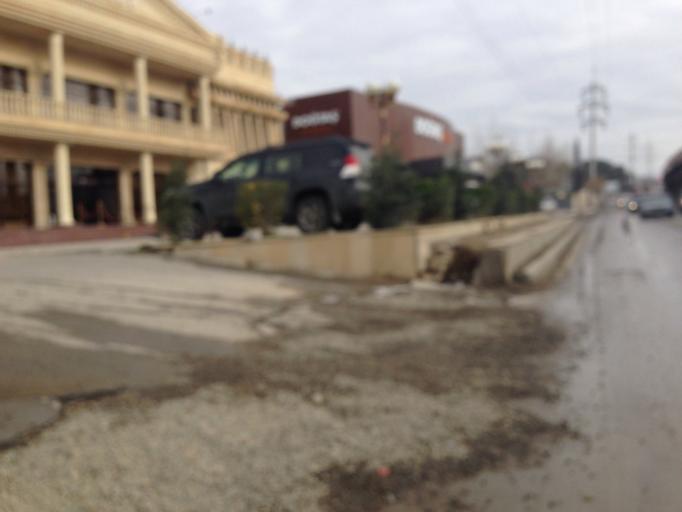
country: AZ
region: Baki
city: Baku
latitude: 40.3892
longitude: 49.8738
